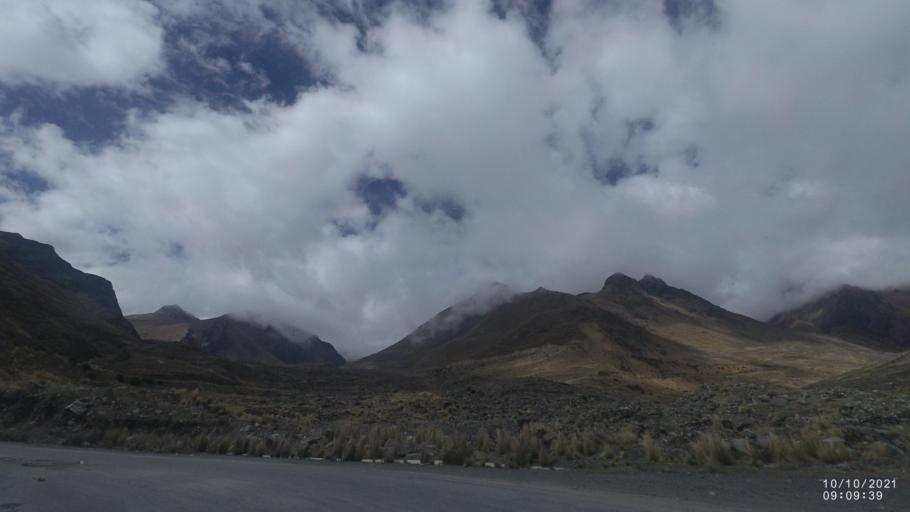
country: BO
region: La Paz
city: Quime
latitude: -17.0242
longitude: -67.2832
